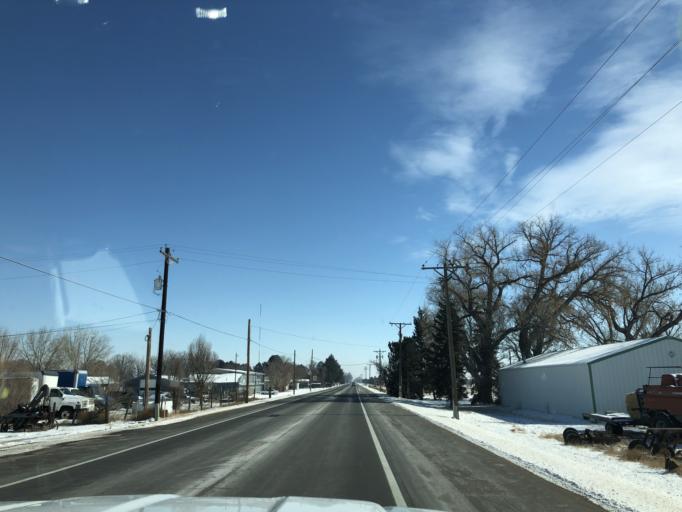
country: US
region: Colorado
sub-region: Morgan County
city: Fort Morgan
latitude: 40.2540
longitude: -103.8531
